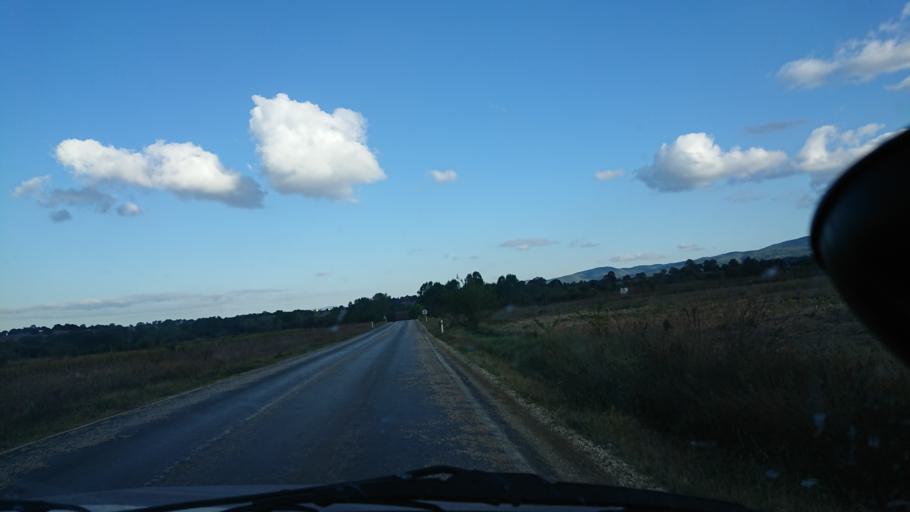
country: TR
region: Bilecik
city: Pazaryeri
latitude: 40.0135
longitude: 29.8511
